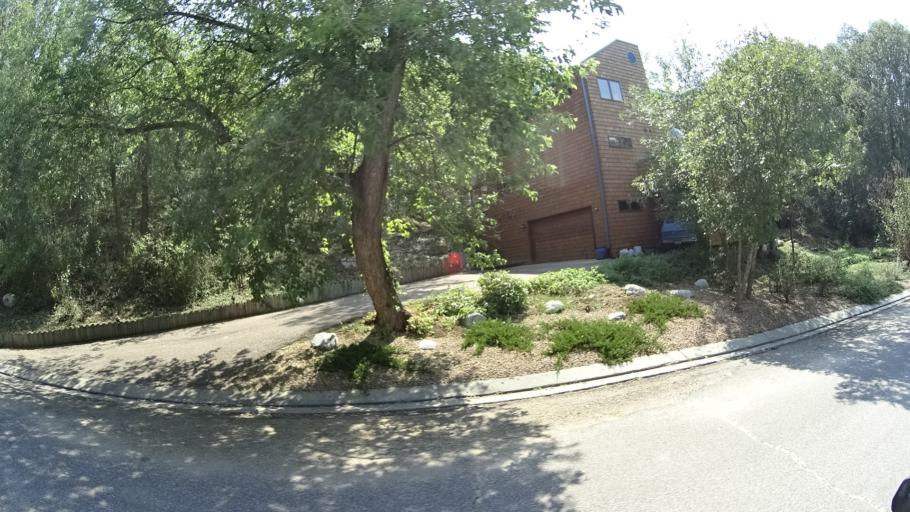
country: US
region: Colorado
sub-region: El Paso County
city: Colorado Springs
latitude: 38.7993
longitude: -104.8390
